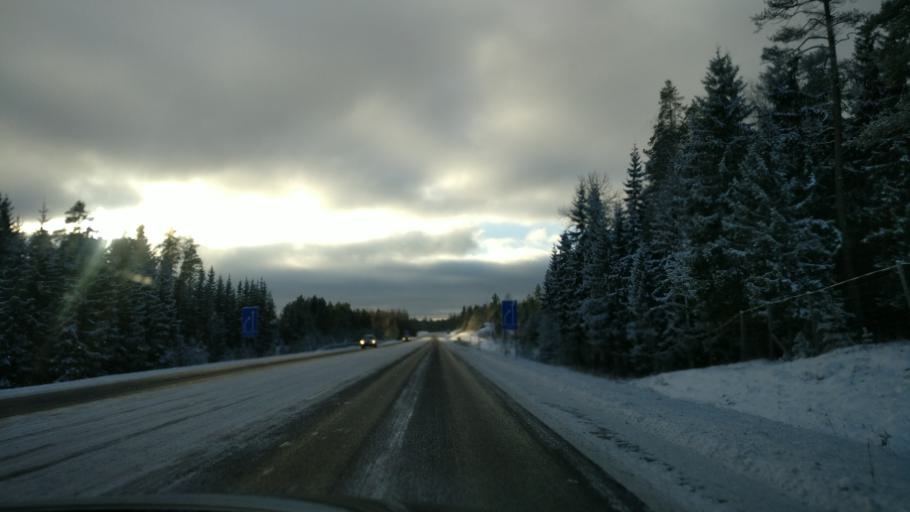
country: FI
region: Paijanne Tavastia
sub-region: Lahti
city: Heinola
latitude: 61.3558
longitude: 26.2291
